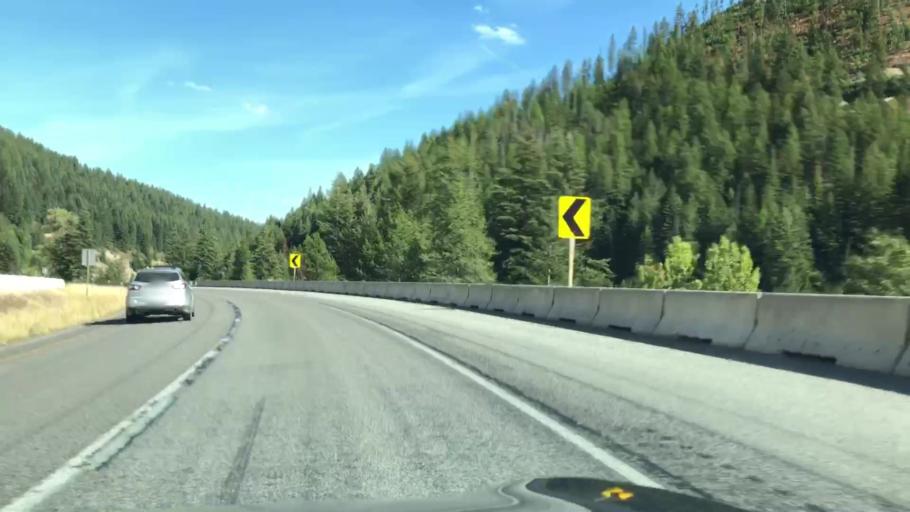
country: US
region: Montana
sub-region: Sanders County
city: Thompson Falls
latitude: 47.4010
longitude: -115.4719
